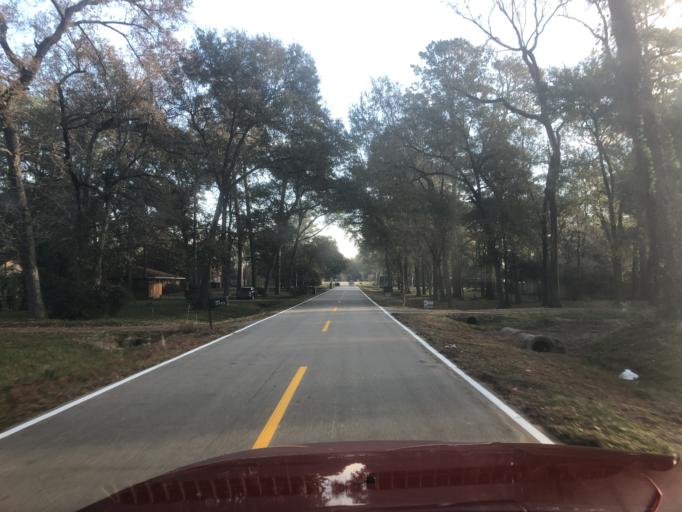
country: US
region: Texas
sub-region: Harris County
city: Spring
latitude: 30.0192
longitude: -95.4754
